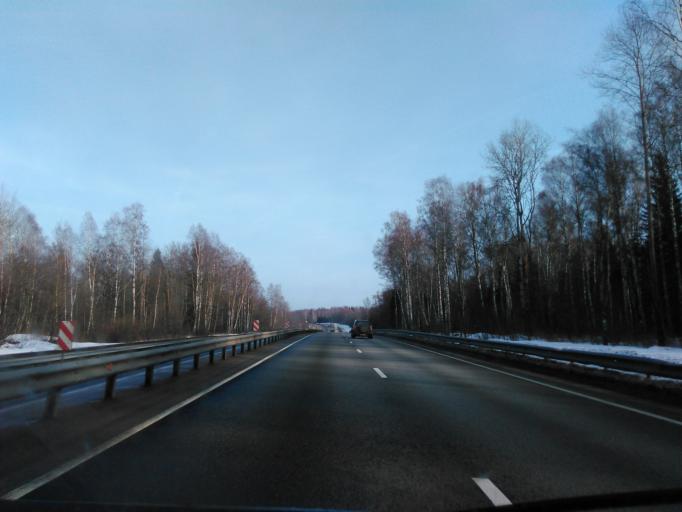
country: RU
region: Smolensk
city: Vyaz'ma
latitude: 55.1928
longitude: 33.9457
